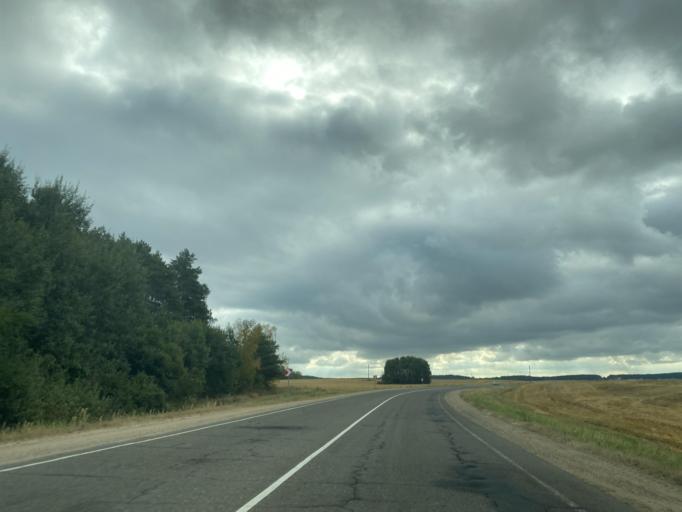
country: BY
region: Minsk
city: Bal'shavik
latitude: 53.9822
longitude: 27.5687
